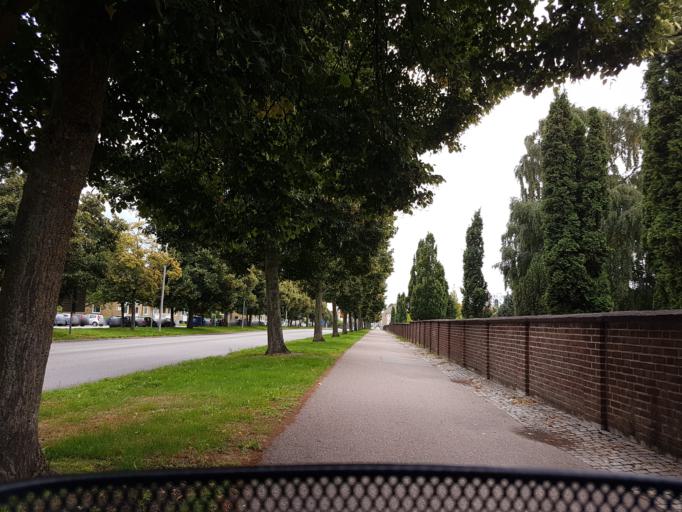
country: SE
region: Skane
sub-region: Landskrona
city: Landskrona
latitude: 55.8842
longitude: 12.8316
